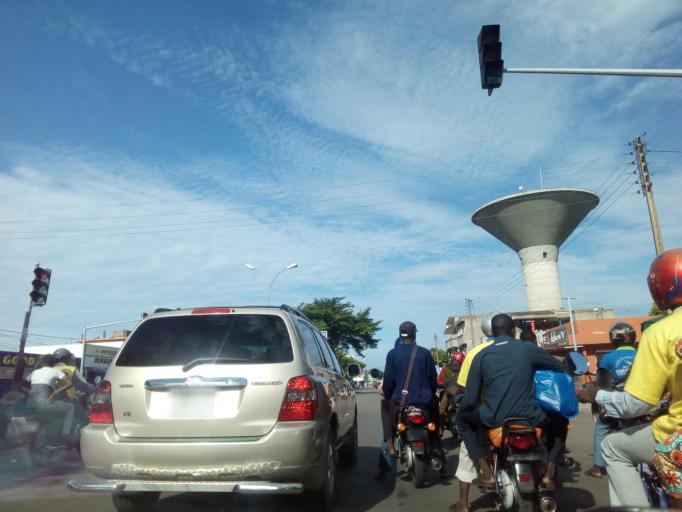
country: BJ
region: Littoral
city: Cotonou
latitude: 6.3624
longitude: 2.4239
